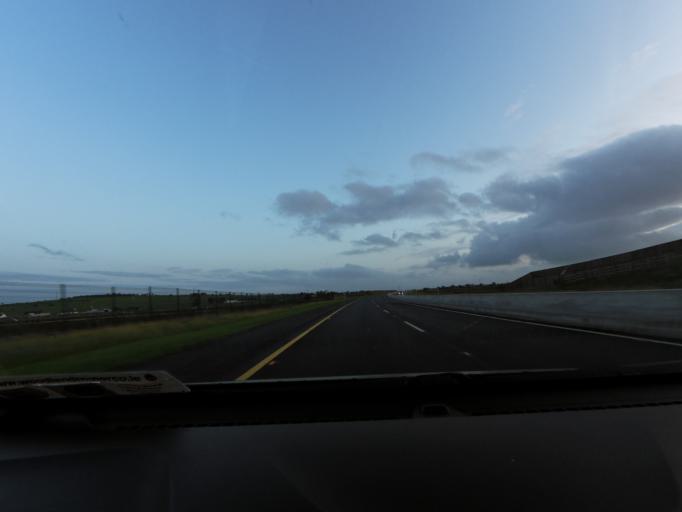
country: IE
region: Connaught
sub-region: County Galway
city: Athenry
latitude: 53.3925
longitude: -8.8031
